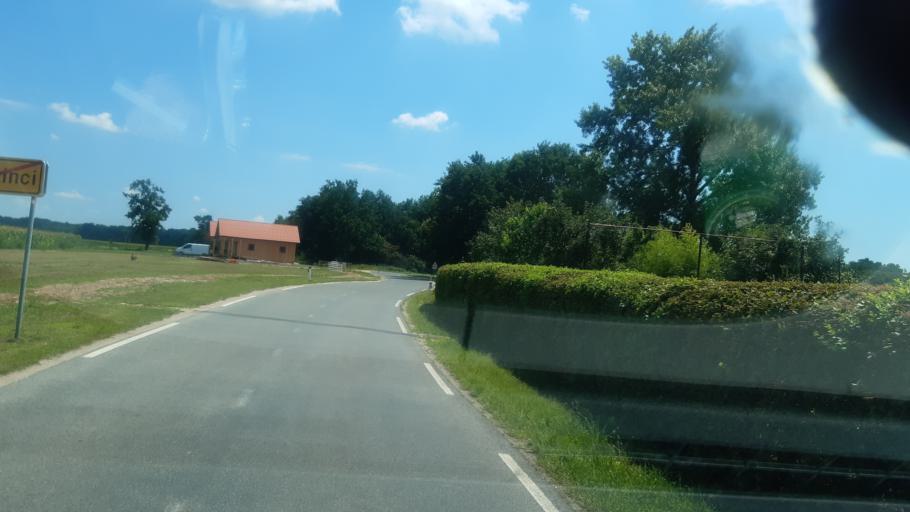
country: SI
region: Moravske Toplice
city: Moravske Toplice
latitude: 46.6672
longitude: 16.2285
